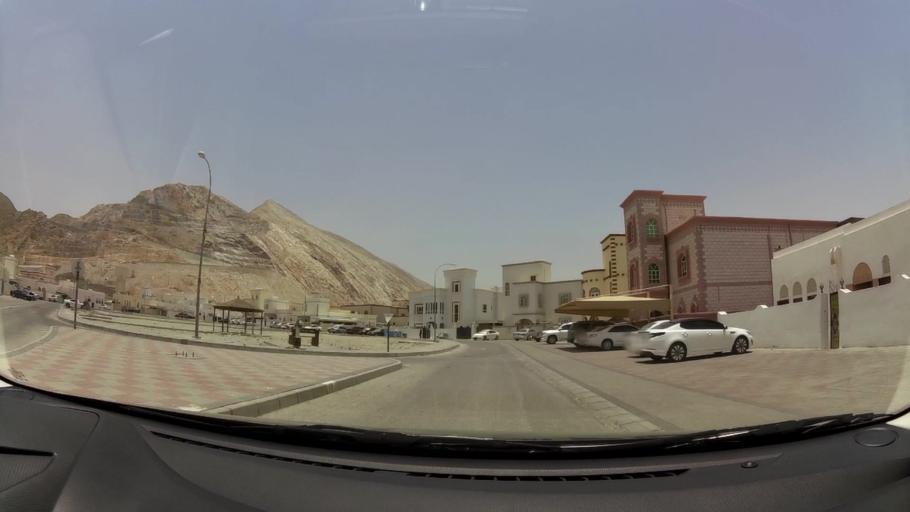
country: OM
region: Muhafazat Masqat
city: Bawshar
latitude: 23.5677
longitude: 58.4255
